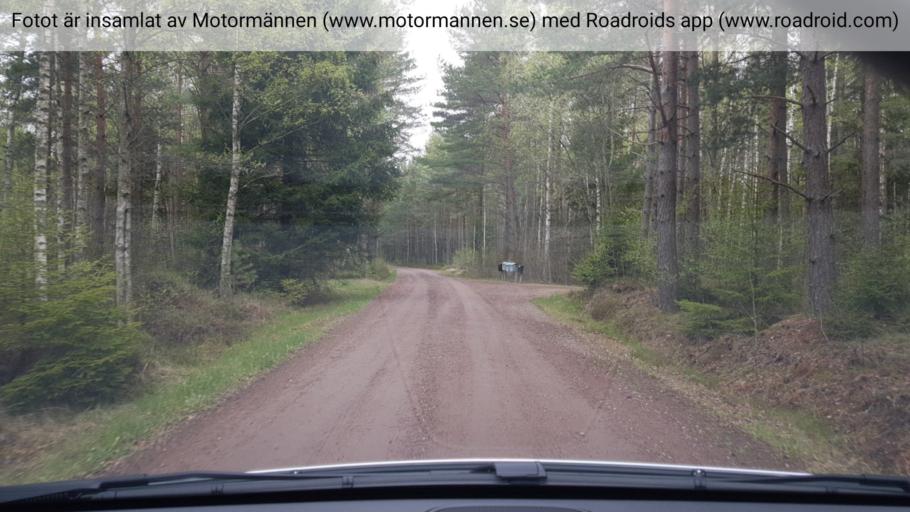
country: SE
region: Vaestra Goetaland
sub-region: Skovde Kommun
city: Stopen
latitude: 58.4504
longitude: 13.9491
